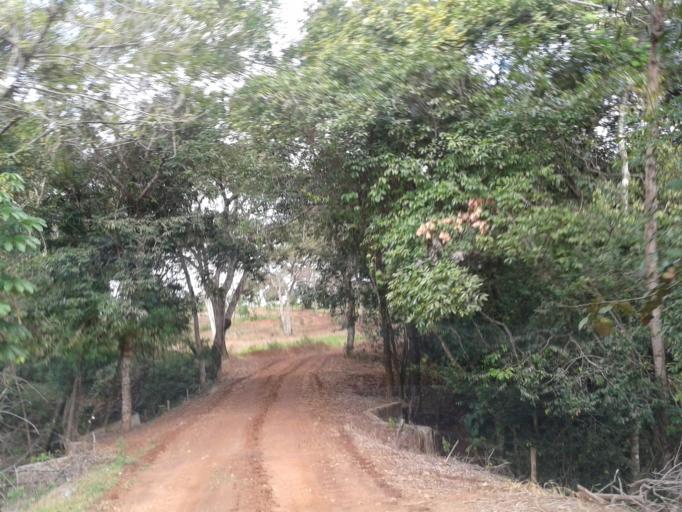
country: BR
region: Minas Gerais
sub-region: Campina Verde
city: Campina Verde
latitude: -19.3852
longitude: -49.6612
